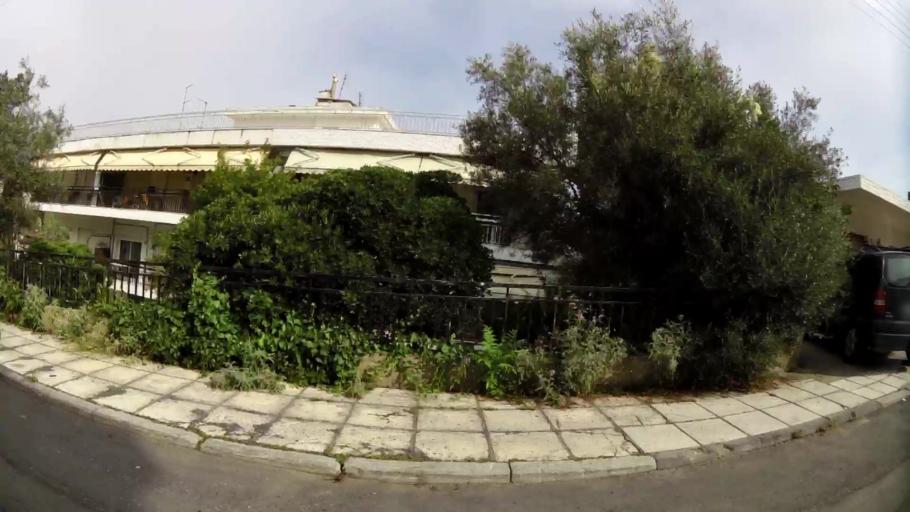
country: GR
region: Central Macedonia
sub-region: Nomos Thessalonikis
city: Panorama
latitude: 40.5917
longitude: 23.0419
